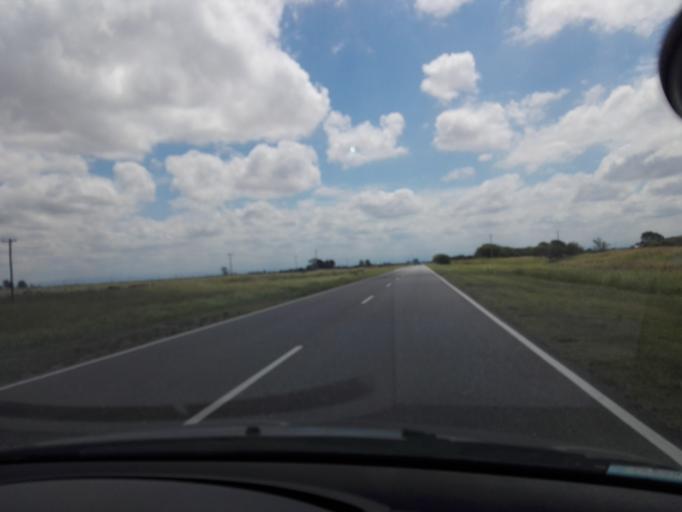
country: AR
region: Cordoba
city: Toledo
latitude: -31.6464
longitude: -64.0483
